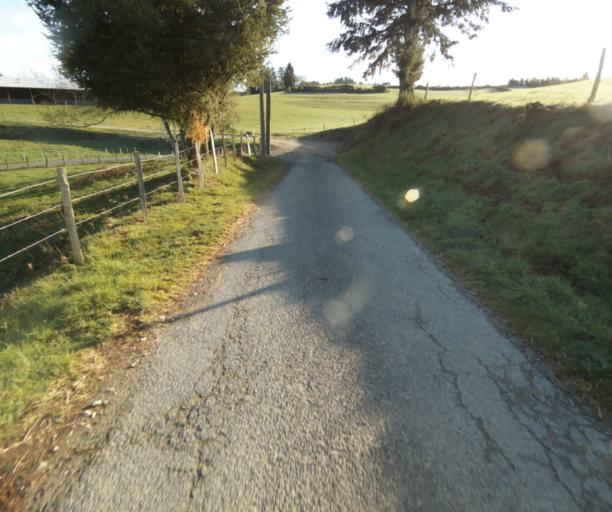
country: FR
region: Limousin
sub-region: Departement de la Correze
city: Correze
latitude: 45.3769
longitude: 1.8555
